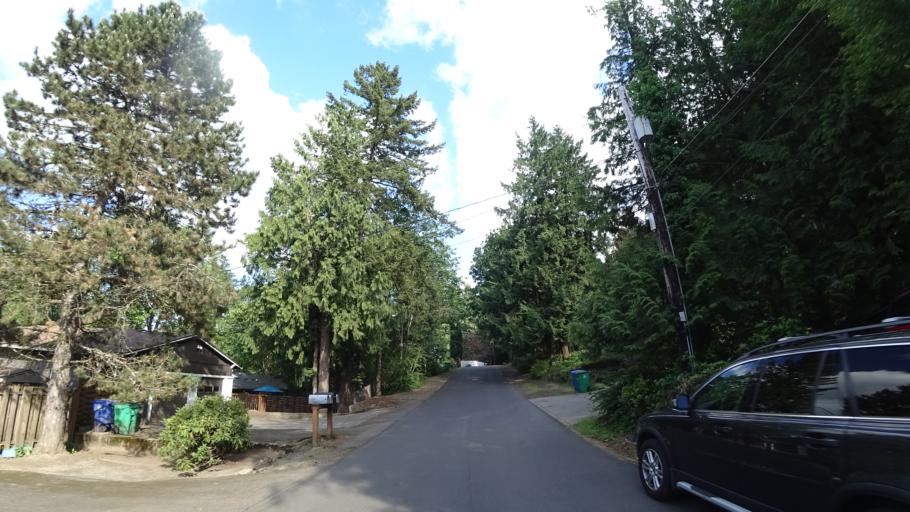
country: US
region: Oregon
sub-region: Washington County
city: Raleigh Hills
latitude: 45.4820
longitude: -122.7178
